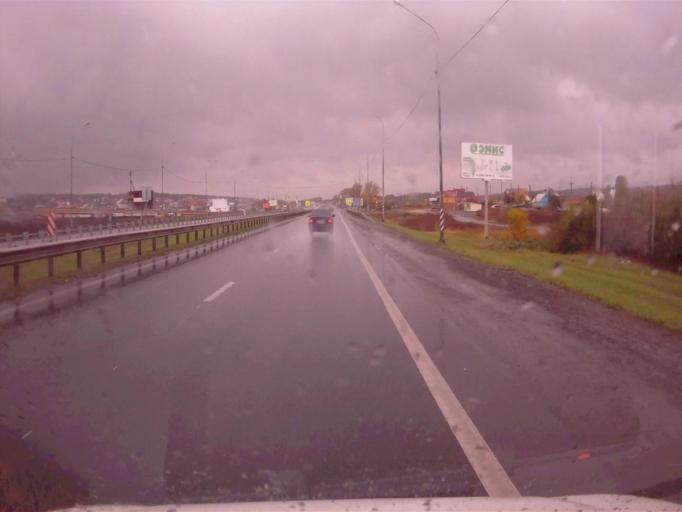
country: RU
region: Chelyabinsk
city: Dolgoderevenskoye
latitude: 55.2717
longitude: 61.3441
